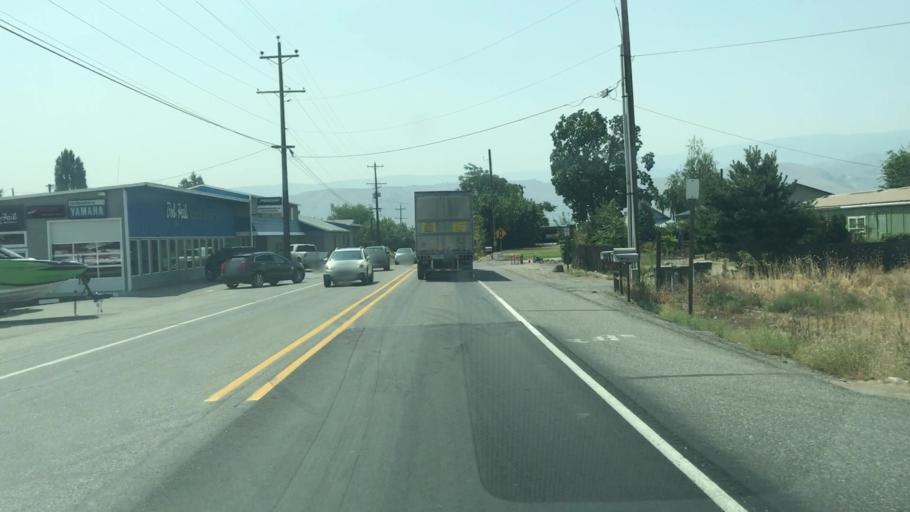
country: US
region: Washington
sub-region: Chelan County
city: Wenatchee
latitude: 47.4407
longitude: -120.2975
